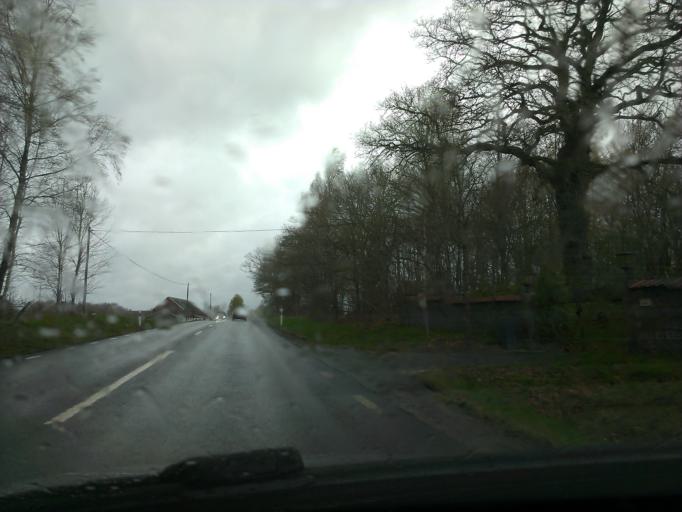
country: SE
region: Skane
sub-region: Ostra Goinge Kommun
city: Knislinge
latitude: 56.1732
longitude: 14.0971
